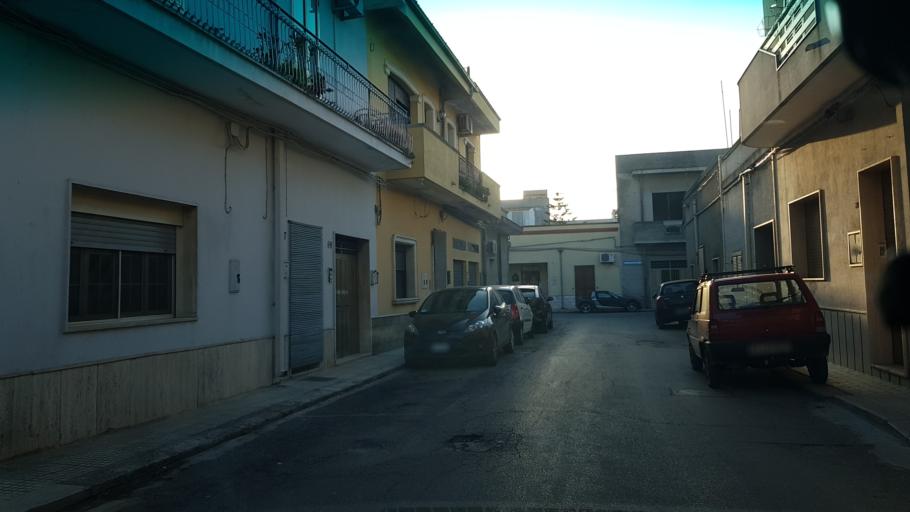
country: IT
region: Apulia
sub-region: Provincia di Brindisi
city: Mesagne
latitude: 40.5529
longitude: 17.8045
